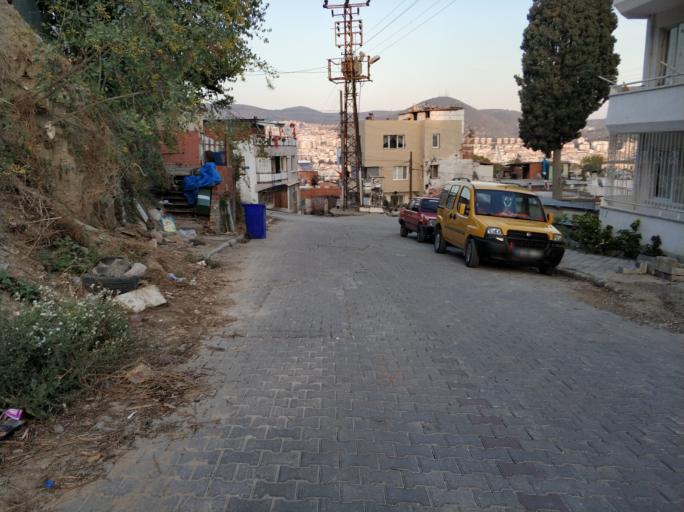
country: TR
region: Aydin
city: Kusadasi
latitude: 37.8575
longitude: 27.2529
